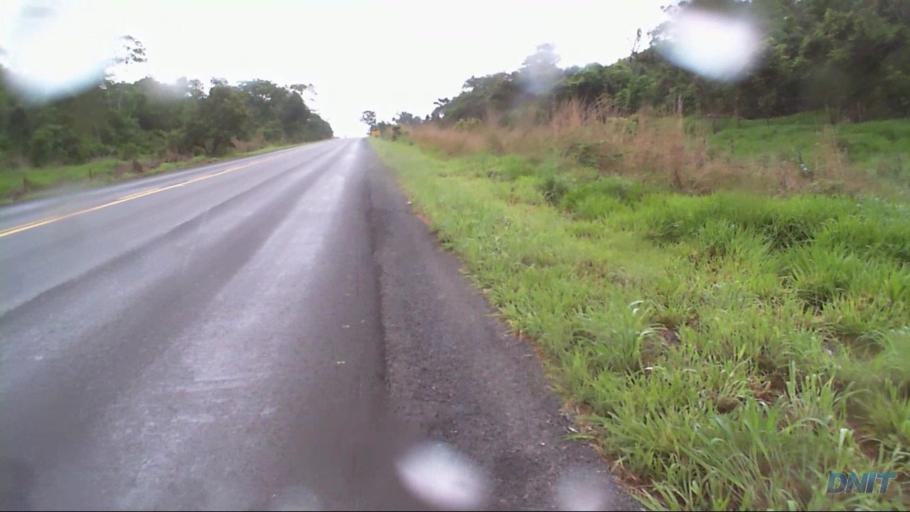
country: BR
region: Goias
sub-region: Padre Bernardo
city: Padre Bernardo
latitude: -15.2044
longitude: -48.4607
